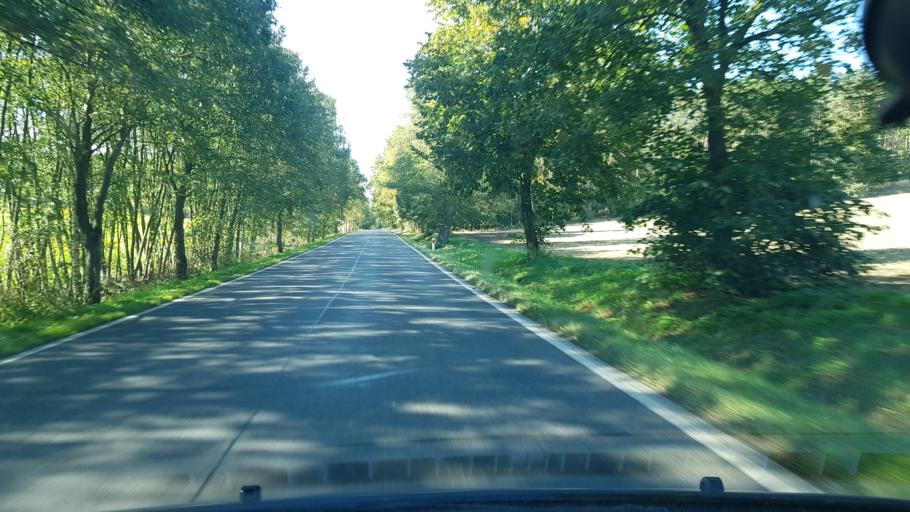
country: CZ
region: Jihocesky
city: Radomysl
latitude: 49.2977
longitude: 14.0148
